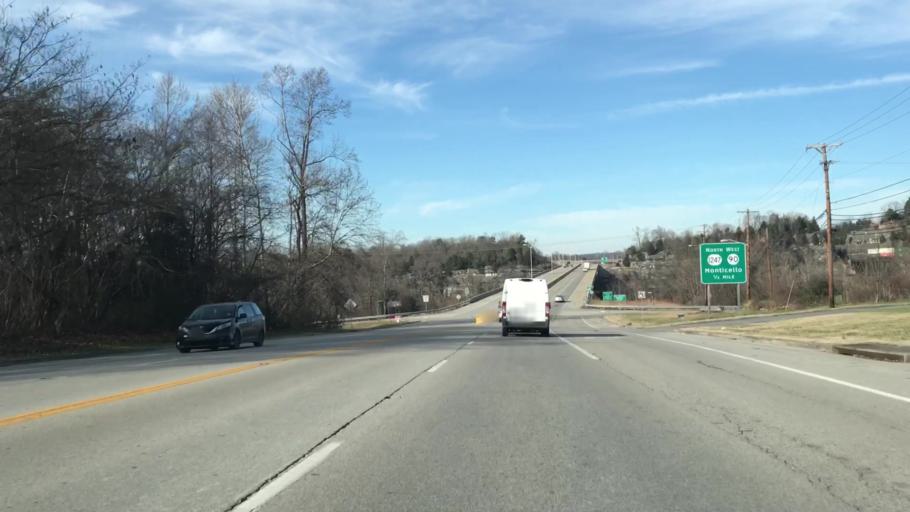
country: US
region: Kentucky
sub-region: Pulaski County
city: Somerset
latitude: 36.9927
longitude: -84.6037
